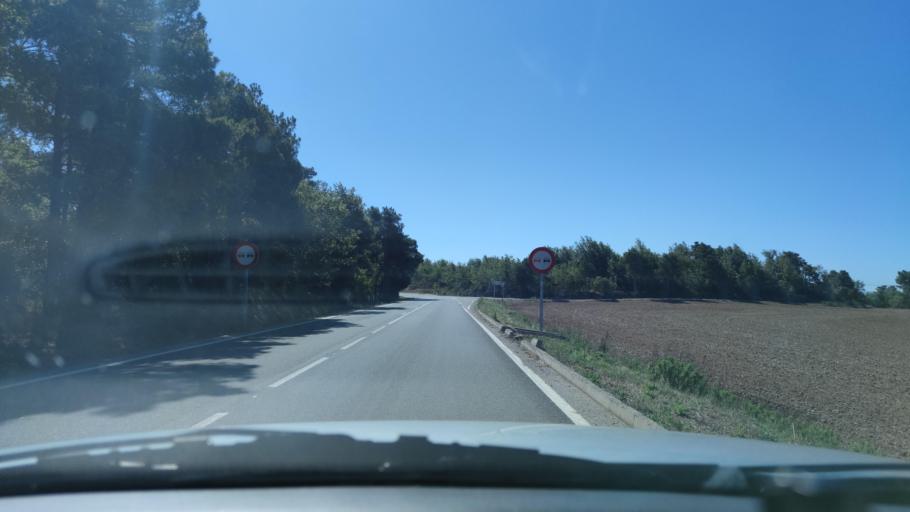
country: ES
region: Catalonia
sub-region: Provincia de Lleida
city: Solsona
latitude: 41.9137
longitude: 1.5109
